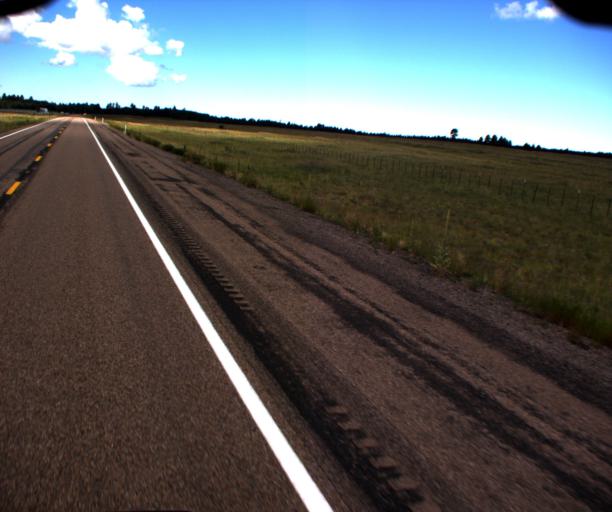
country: US
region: Arizona
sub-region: Apache County
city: Eagar
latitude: 34.0469
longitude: -109.5851
